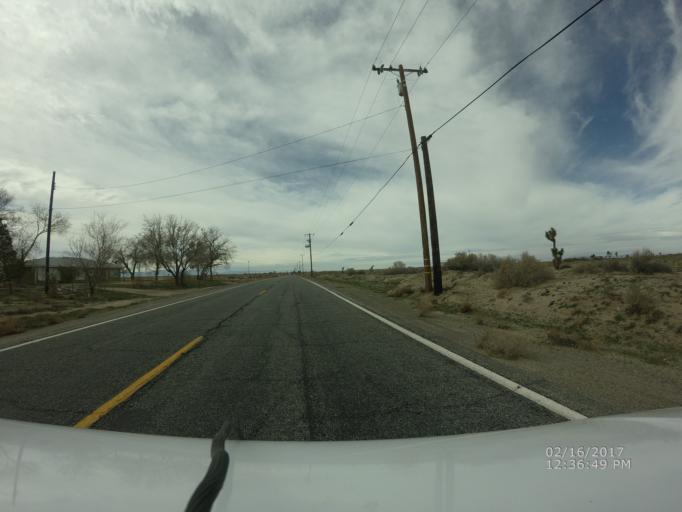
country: US
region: California
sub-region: Los Angeles County
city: Lake Los Angeles
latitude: 34.6755
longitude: -117.8698
